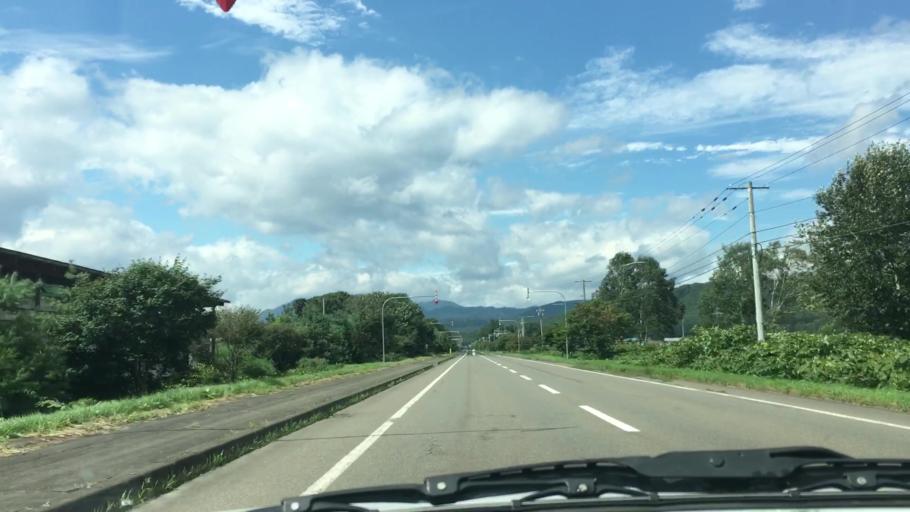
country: JP
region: Hokkaido
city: Otofuke
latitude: 43.3120
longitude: 143.3074
